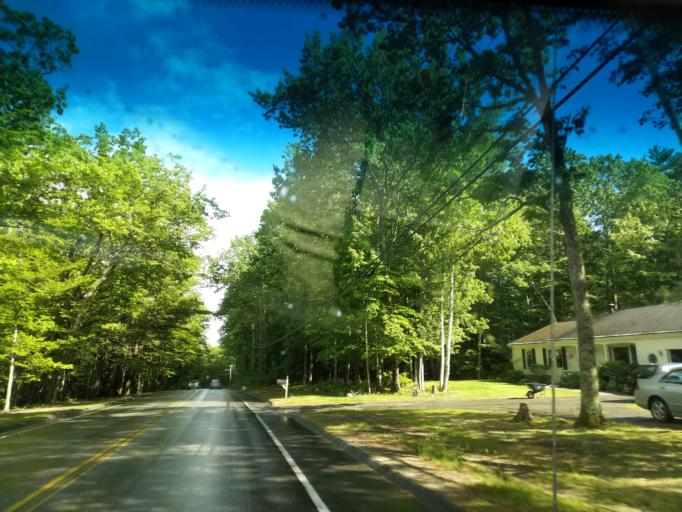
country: US
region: Maine
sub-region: Cumberland County
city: Cumberland Center
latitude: 43.7499
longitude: -70.3139
